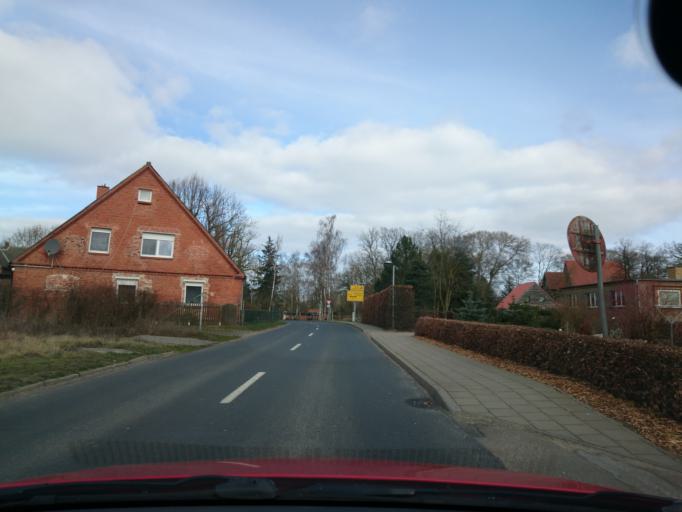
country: DE
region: Mecklenburg-Vorpommern
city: Velgast
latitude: 54.3314
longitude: 12.7968
